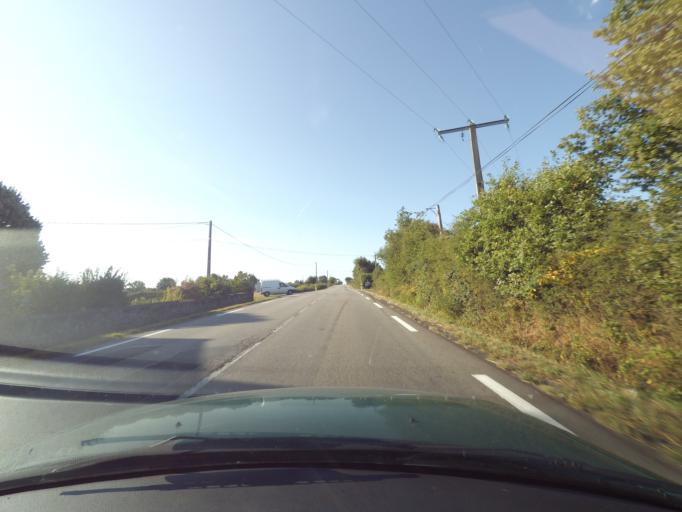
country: FR
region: Poitou-Charentes
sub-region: Departement des Deux-Sevres
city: Chiche
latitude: 46.7571
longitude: -0.3100
